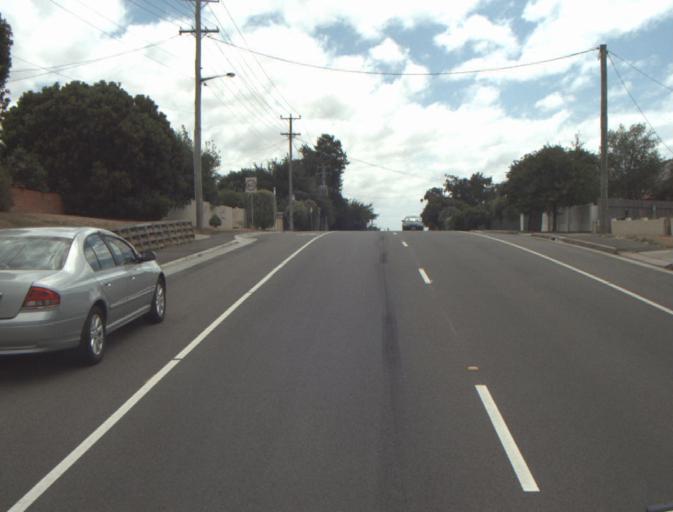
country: AU
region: Tasmania
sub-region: Launceston
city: Newstead
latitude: -41.4585
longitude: 147.1807
